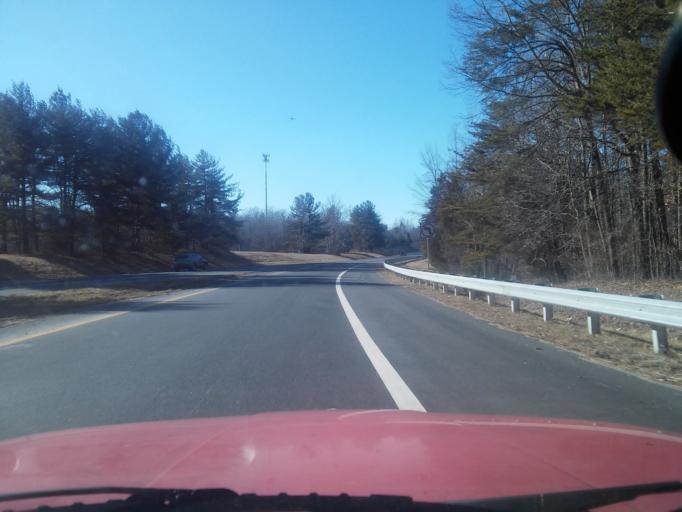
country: US
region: Virginia
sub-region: Fluvanna County
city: Palmyra
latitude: 37.9792
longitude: -78.2176
